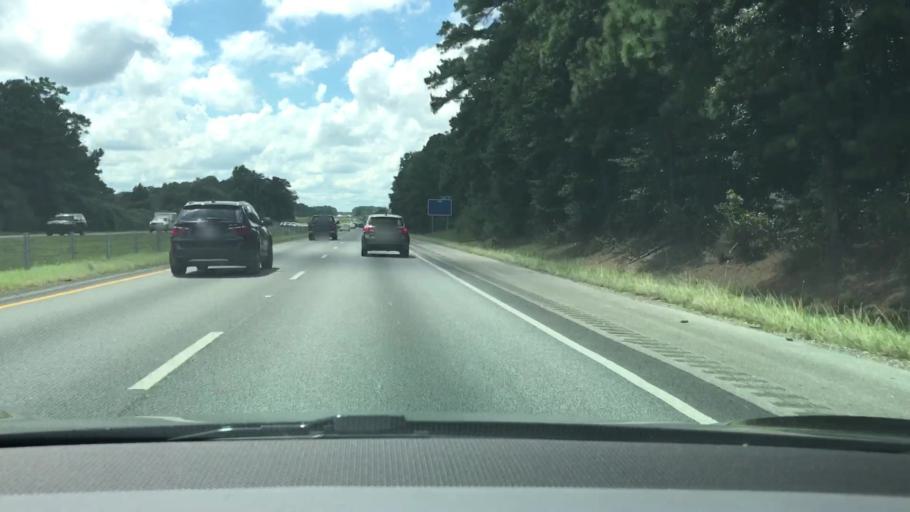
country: US
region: Alabama
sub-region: Lee County
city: Opelika
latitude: 32.6100
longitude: -85.4174
